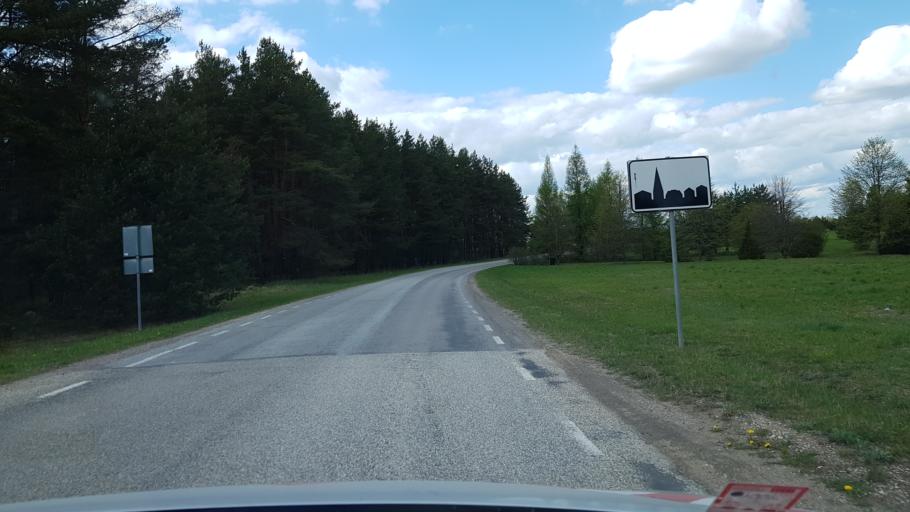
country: EE
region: Tartu
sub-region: Tartu linn
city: Tartu
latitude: 58.3567
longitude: 26.7976
